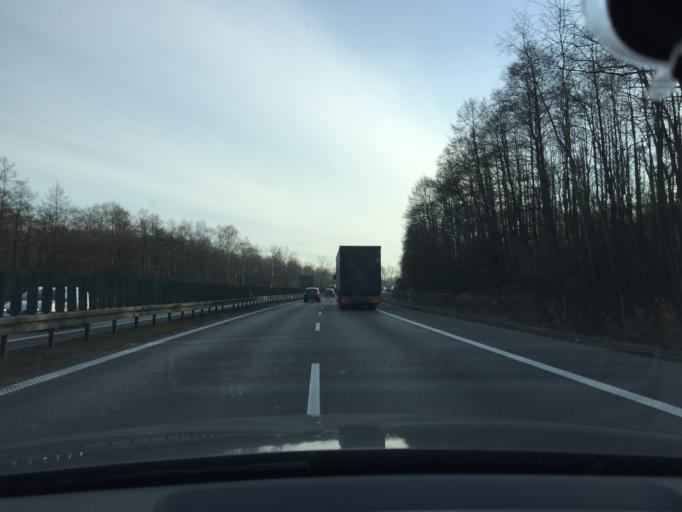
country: PL
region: Lesser Poland Voivodeship
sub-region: Krakow
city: Sidzina
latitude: 50.0131
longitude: 19.8471
